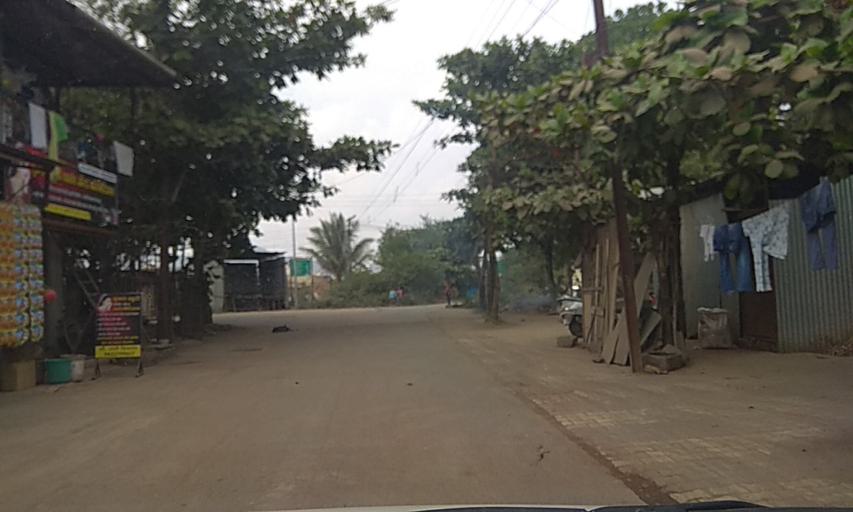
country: IN
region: Maharashtra
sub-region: Pune Division
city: Pimpri
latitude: 18.5769
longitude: 73.7091
